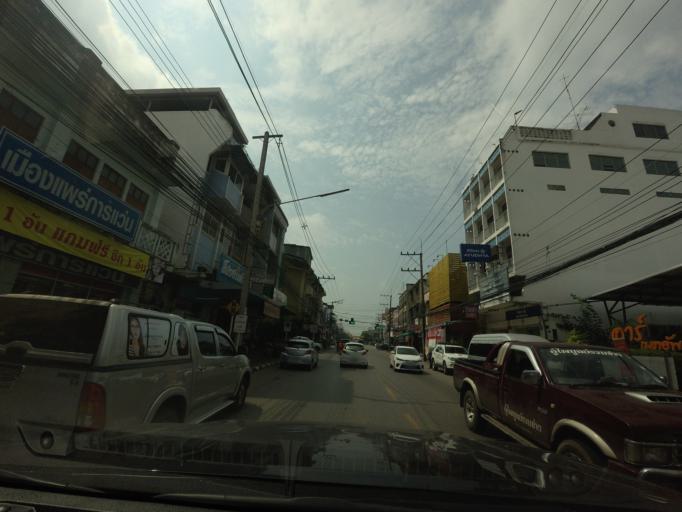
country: TH
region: Phrae
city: Phrae
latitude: 18.1371
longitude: 100.1472
